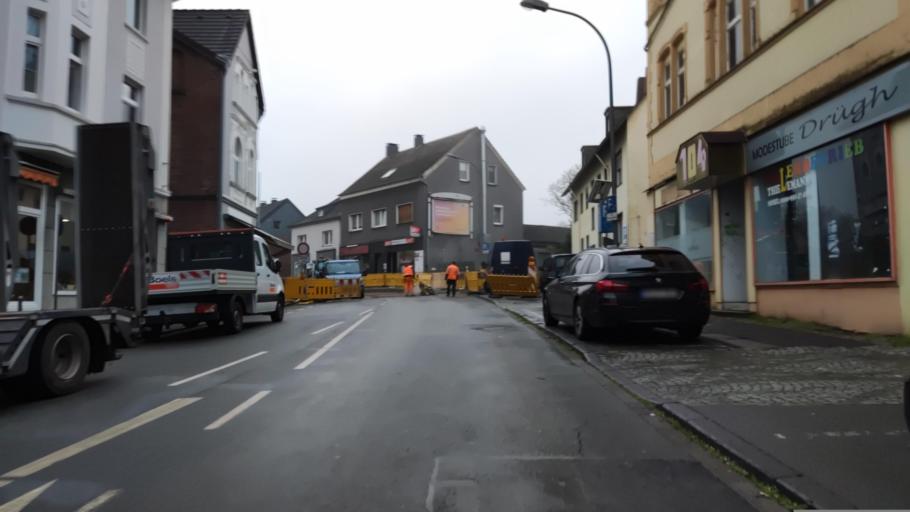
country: DE
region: North Rhine-Westphalia
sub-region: Regierungsbezirk Arnsberg
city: Bochum
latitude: 51.4408
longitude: 7.2103
